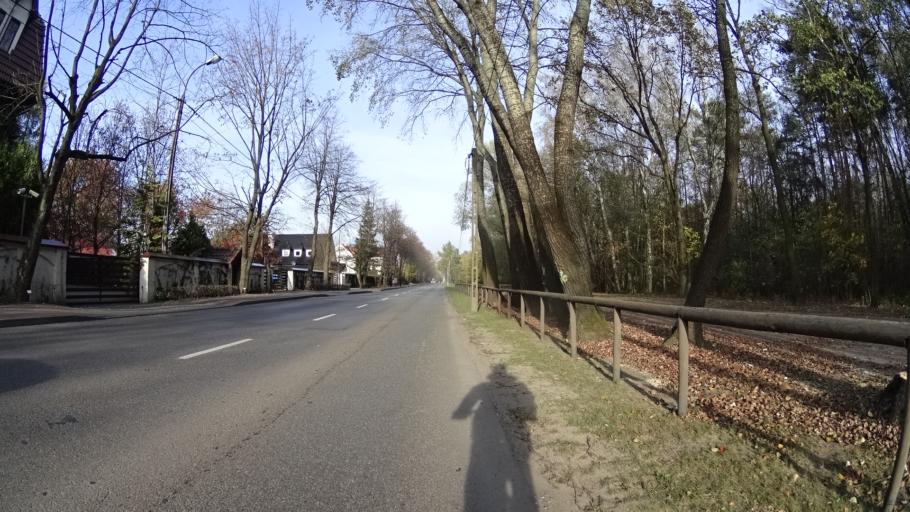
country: PL
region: Masovian Voivodeship
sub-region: Powiat warszawski zachodni
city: Babice
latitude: 52.2611
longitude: 20.8540
